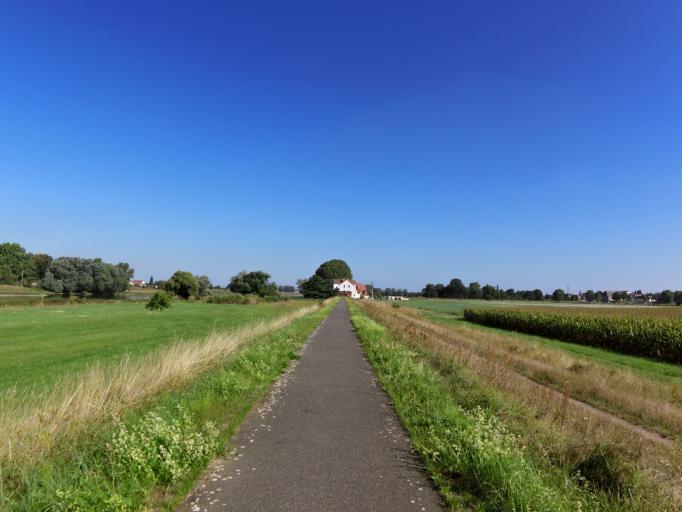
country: DE
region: Saxony
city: Riesa
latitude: 51.3176
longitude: 13.2938
